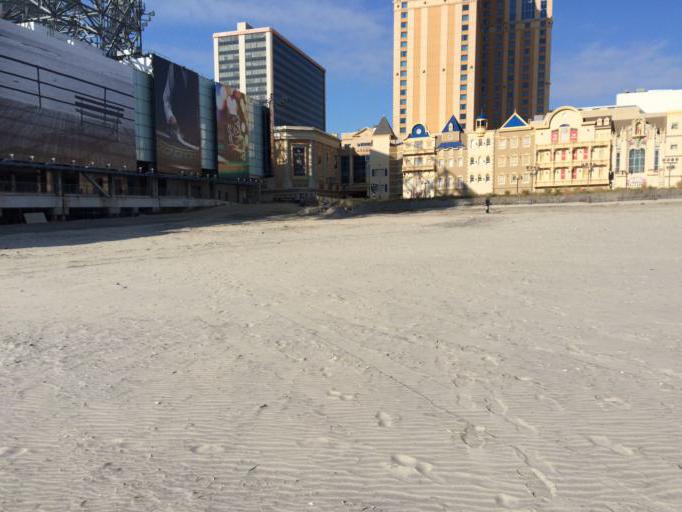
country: US
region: New Jersey
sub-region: Atlantic County
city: Atlantic City
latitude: 39.3542
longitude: -74.4334
